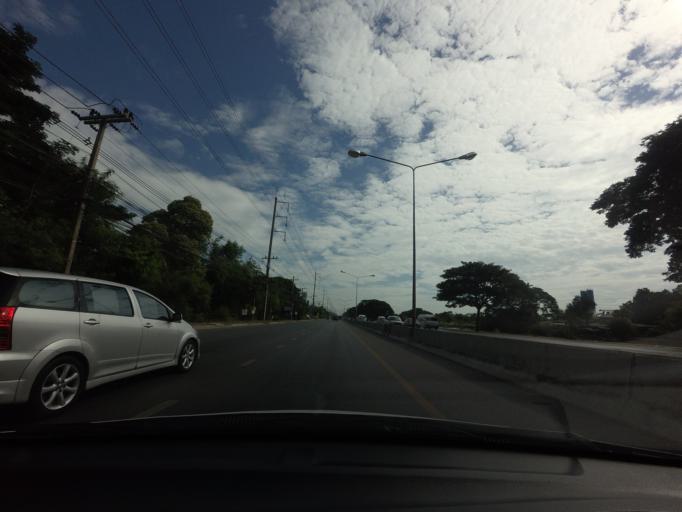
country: TH
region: Pathum Thani
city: Ban Rangsit
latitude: 14.0479
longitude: 100.8099
